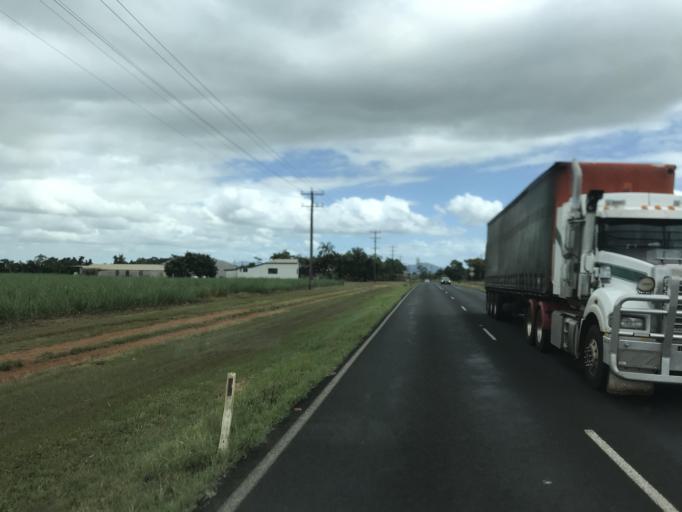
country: AU
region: Queensland
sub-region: Cassowary Coast
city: Innisfail
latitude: -17.5850
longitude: 146.0018
